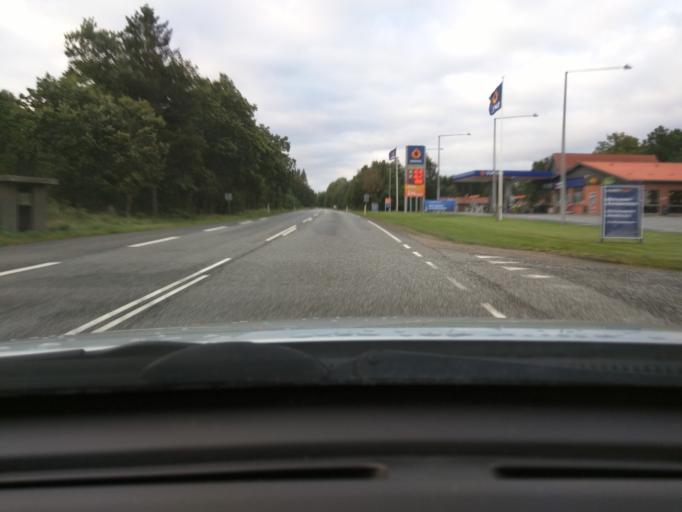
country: DK
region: Central Jutland
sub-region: Ikast-Brande Kommune
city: Bording Kirkeby
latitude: 56.2663
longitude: 9.3140
